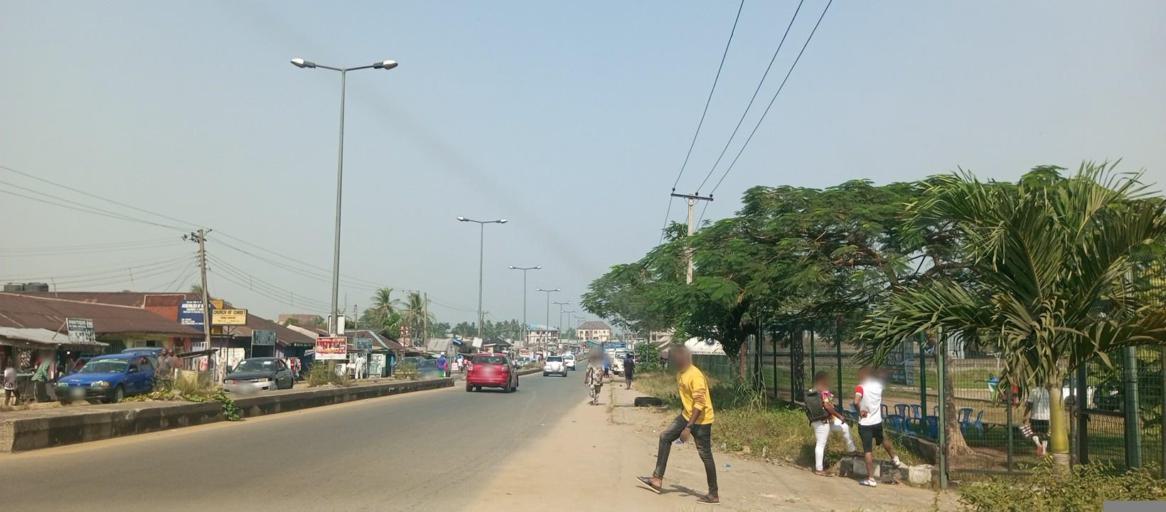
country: NG
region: Rivers
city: Emuoha
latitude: 4.8836
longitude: 6.9046
